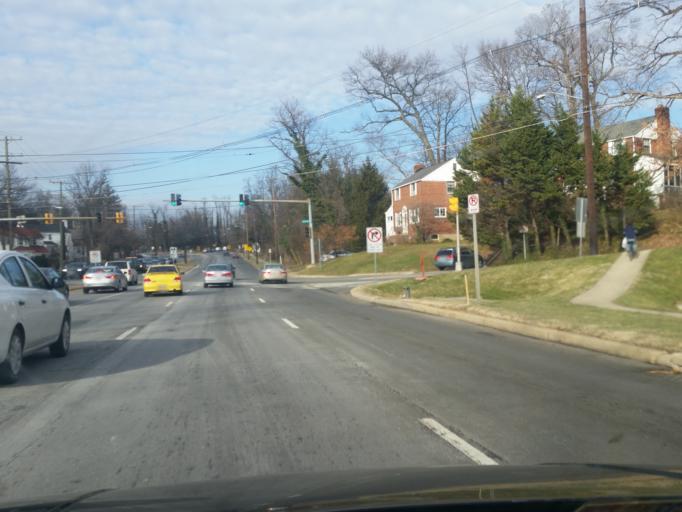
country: US
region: Maryland
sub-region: Montgomery County
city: Silver Spring
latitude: 39.0026
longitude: -77.0401
